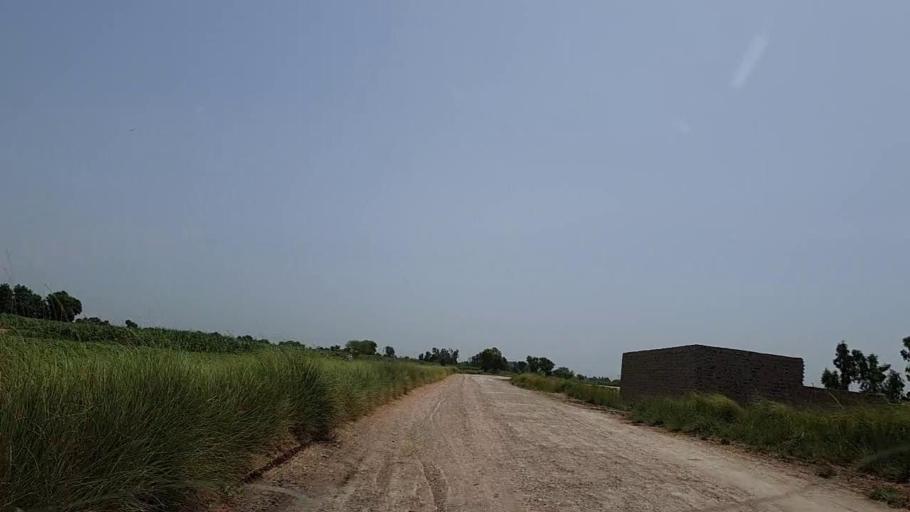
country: PK
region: Sindh
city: Naushahro Firoz
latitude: 26.8435
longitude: 67.9922
